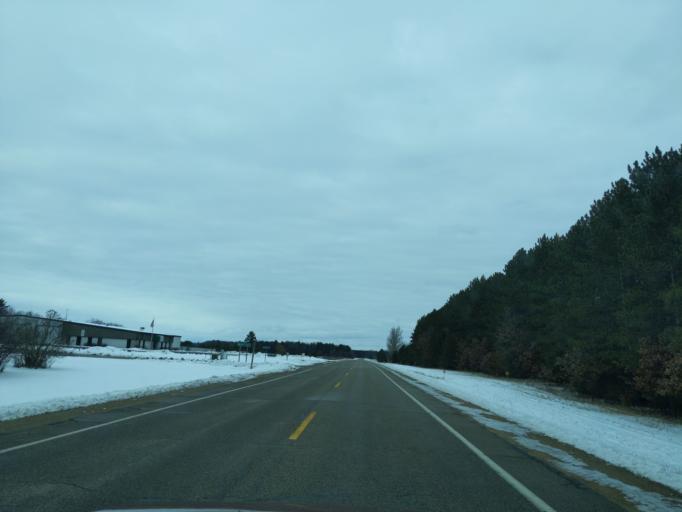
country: US
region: Wisconsin
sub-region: Waushara County
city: Wautoma
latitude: 44.0327
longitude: -89.2980
